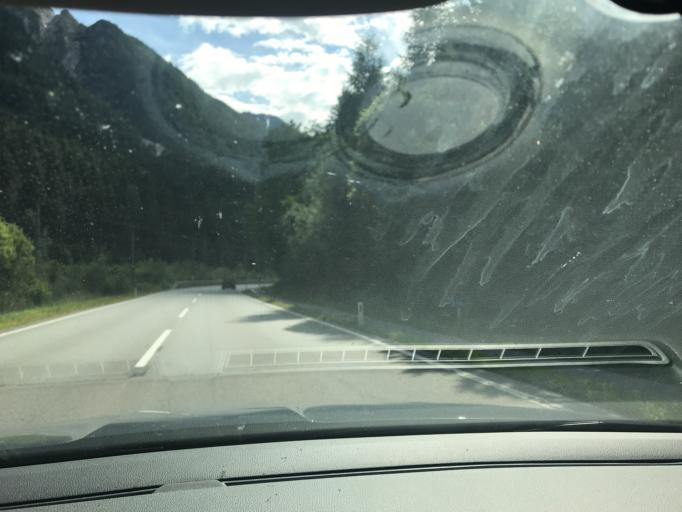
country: AT
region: Tyrol
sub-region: Politischer Bezirk Lienz
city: Obertilliach
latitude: 46.7826
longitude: 12.6554
